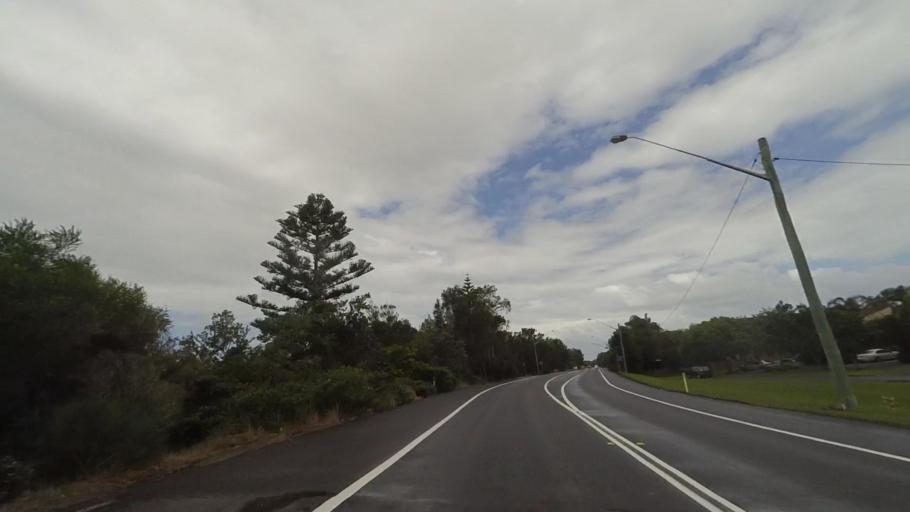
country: AU
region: New South Wales
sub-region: Wyong Shire
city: The Entrance
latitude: -33.3270
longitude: 151.5046
